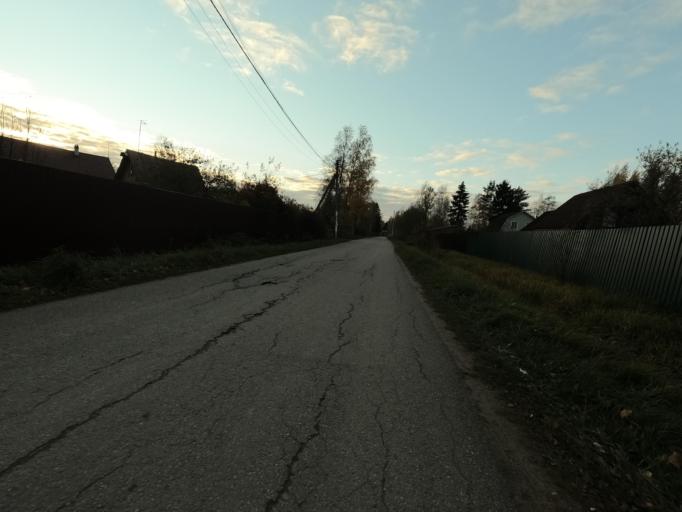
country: RU
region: Leningrad
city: Mga
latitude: 59.7761
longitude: 31.2098
